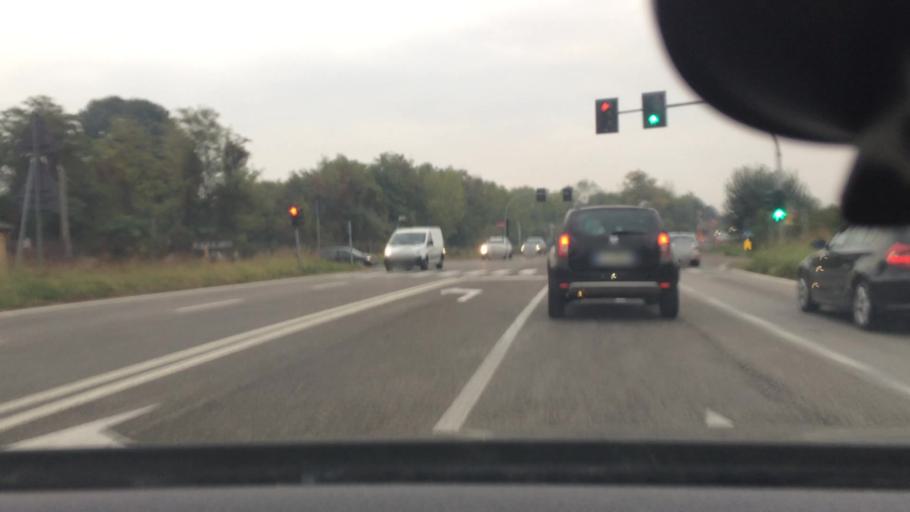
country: IT
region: Lombardy
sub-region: Citta metropolitana di Milano
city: Passirana
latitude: 45.5382
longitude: 9.0462
